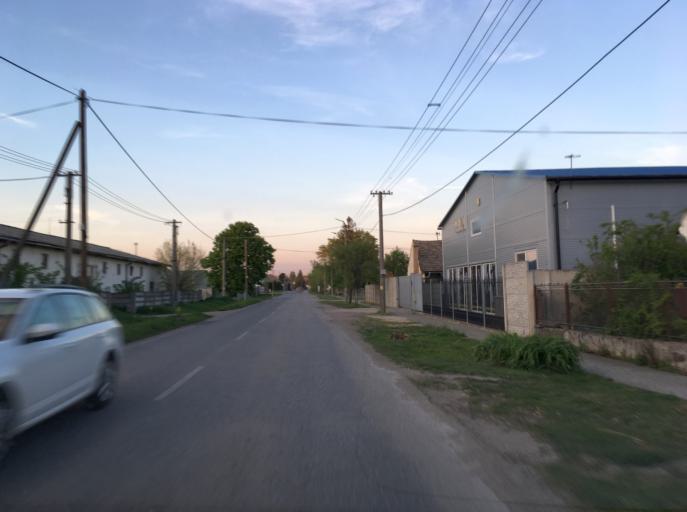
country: SK
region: Nitriansky
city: Kolarovo
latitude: 47.9089
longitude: 17.9834
